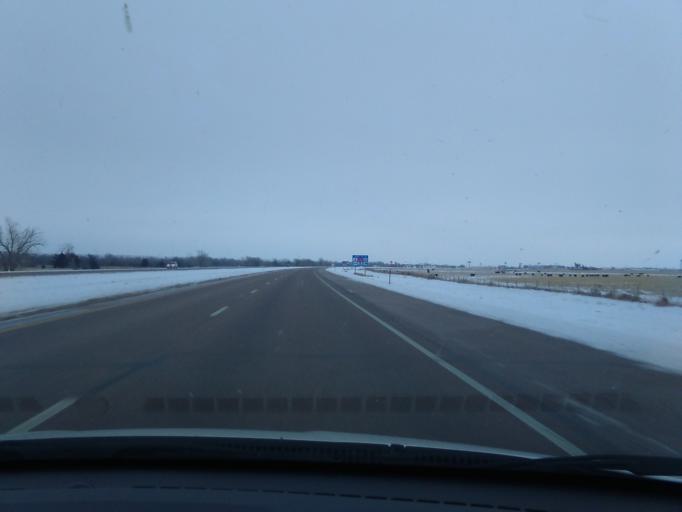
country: US
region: Nebraska
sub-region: Keith County
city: Ogallala
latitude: 41.1119
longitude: -101.7457
